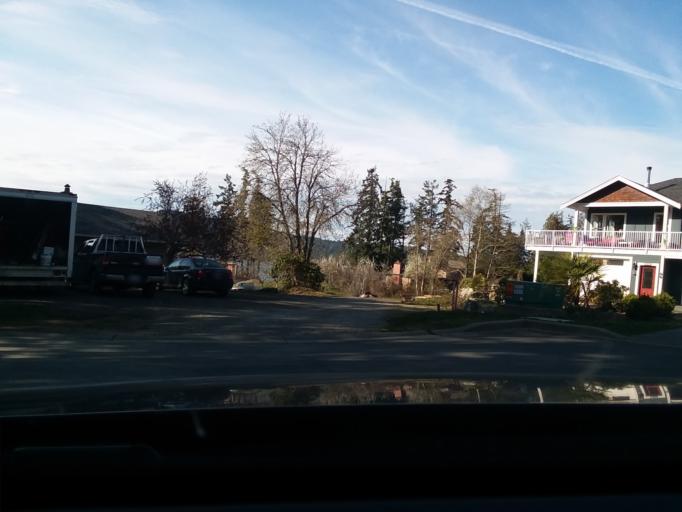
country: CA
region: British Columbia
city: Sooke
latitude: 48.3901
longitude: -123.6676
